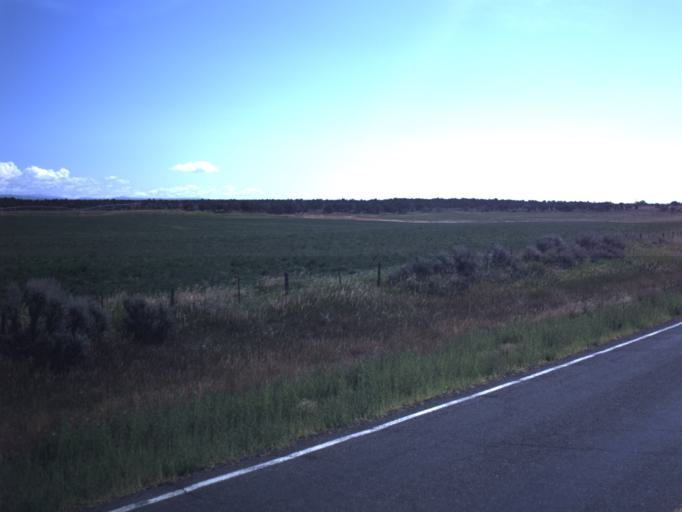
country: US
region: Utah
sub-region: Duchesne County
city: Duchesne
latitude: 40.3557
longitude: -110.3842
